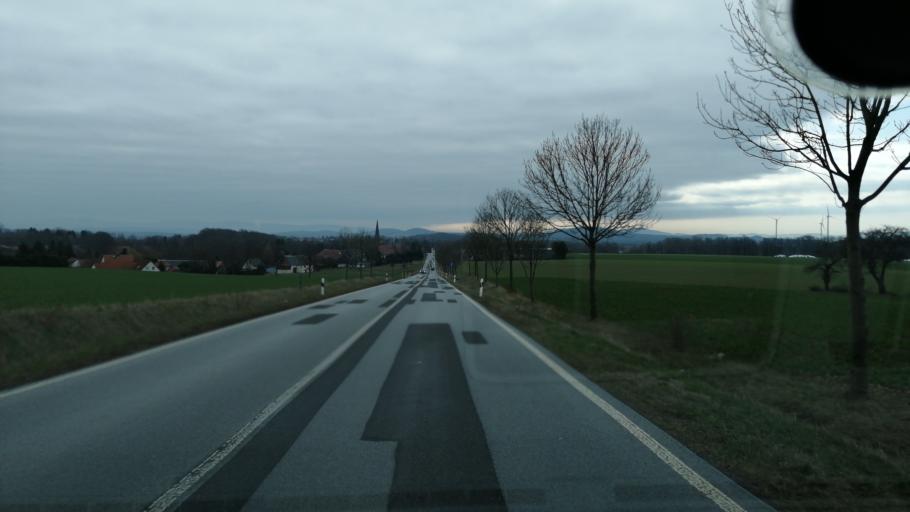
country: DE
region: Saxony
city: Herrnhut
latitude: 51.0353
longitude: 14.7134
